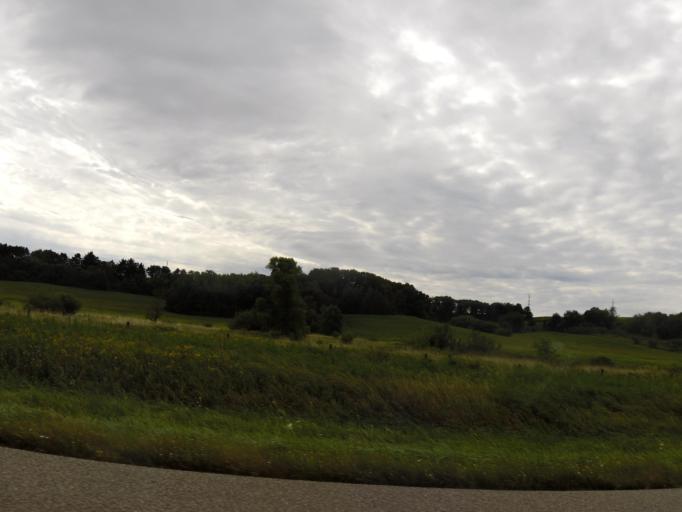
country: US
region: Wisconsin
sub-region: Monroe County
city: Tomah
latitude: 43.9466
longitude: -90.5577
